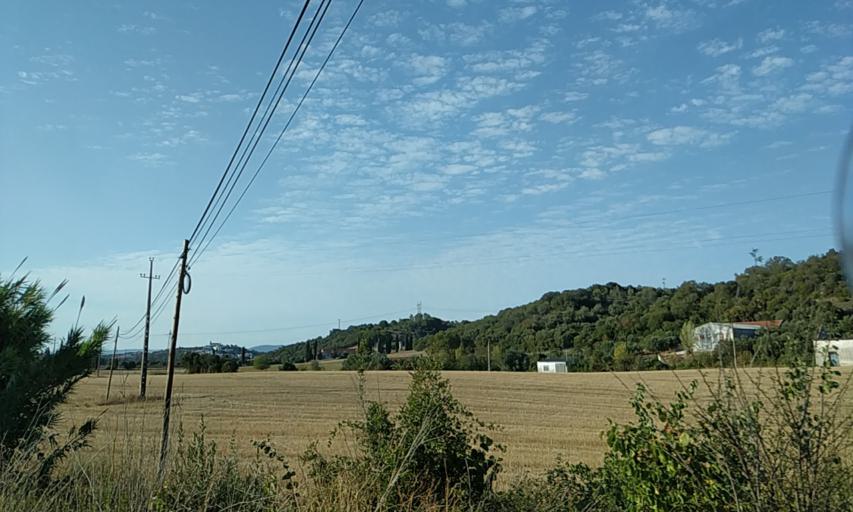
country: PT
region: Santarem
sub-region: Alcanena
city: Alcanena
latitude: 39.3657
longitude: -8.6554
